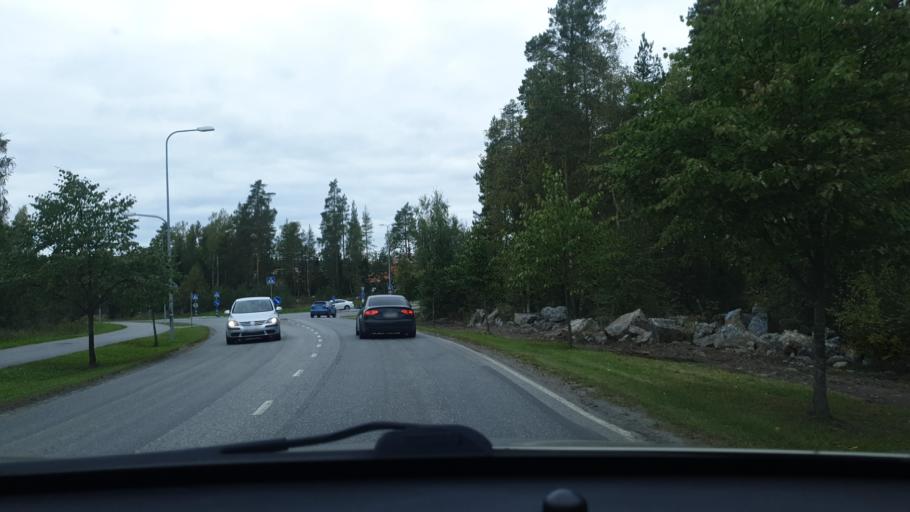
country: FI
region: Ostrobothnia
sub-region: Vaasa
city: Korsholm
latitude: 63.1191
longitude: 21.6581
